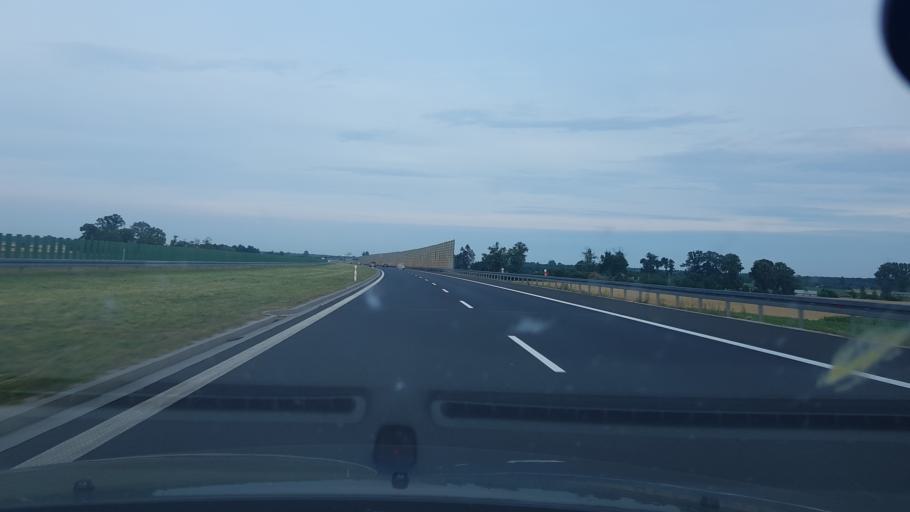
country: PL
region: Lodz Voivodeship
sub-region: Powiat kutnowski
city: Lanieta
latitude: 52.3865
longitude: 19.2957
